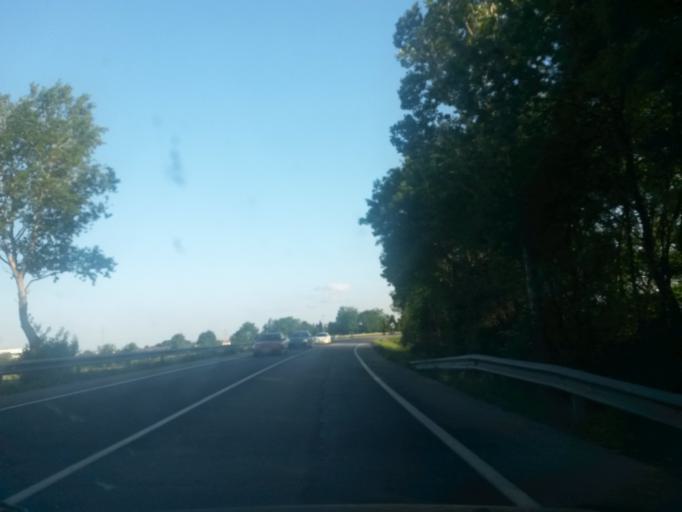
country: ES
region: Catalonia
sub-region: Provincia de Girona
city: Banyoles
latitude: 42.1503
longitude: 2.7621
